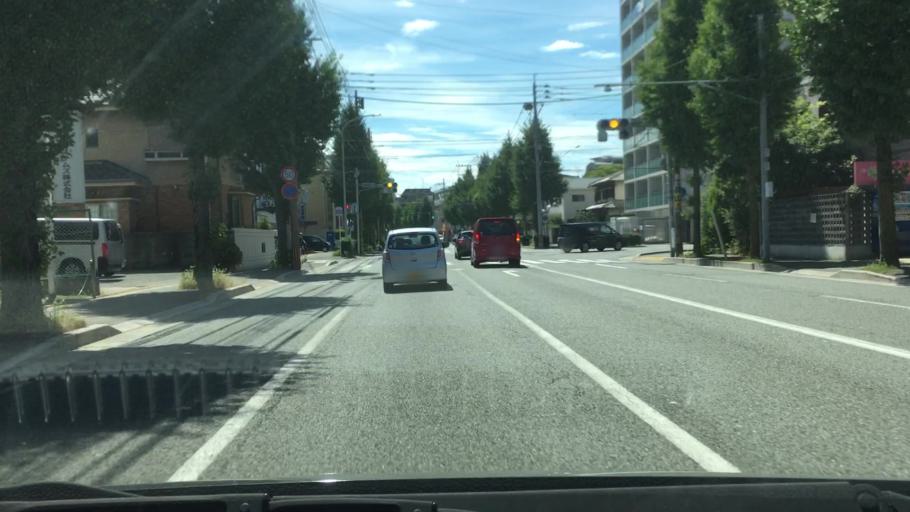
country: JP
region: Fukuoka
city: Fukuoka-shi
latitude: 33.5666
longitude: 130.4276
